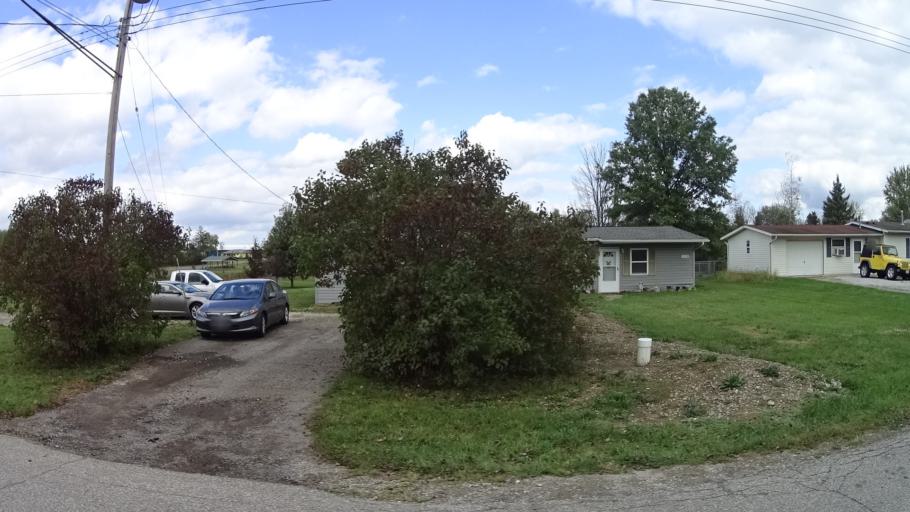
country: US
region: Ohio
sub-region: Lorain County
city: Eaton Estates
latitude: 41.3125
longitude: -82.0080
